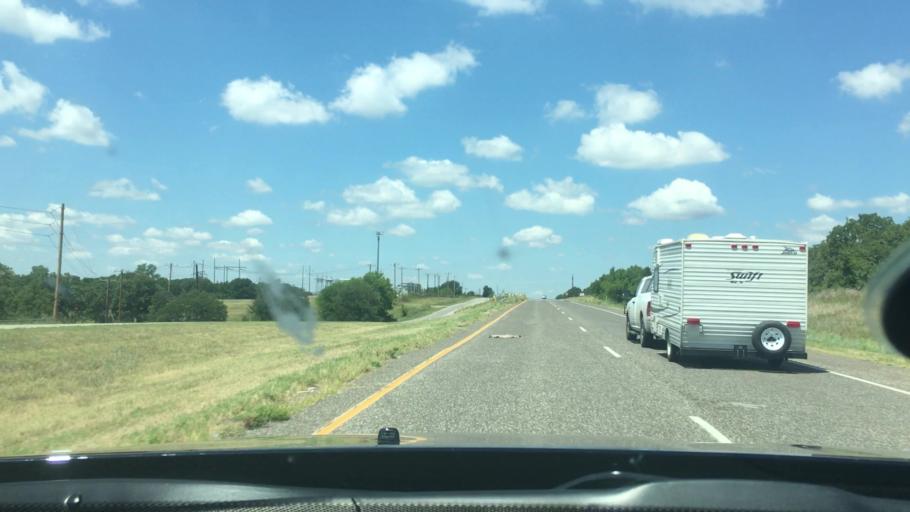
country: US
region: Oklahoma
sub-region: Carter County
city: Lone Grove
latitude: 34.1730
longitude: -97.3275
